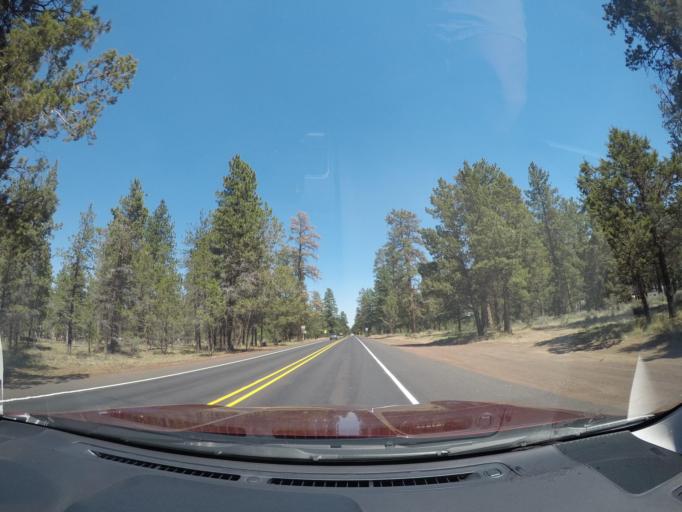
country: US
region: Oregon
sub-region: Deschutes County
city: Sisters
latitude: 44.2877
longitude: -121.5357
